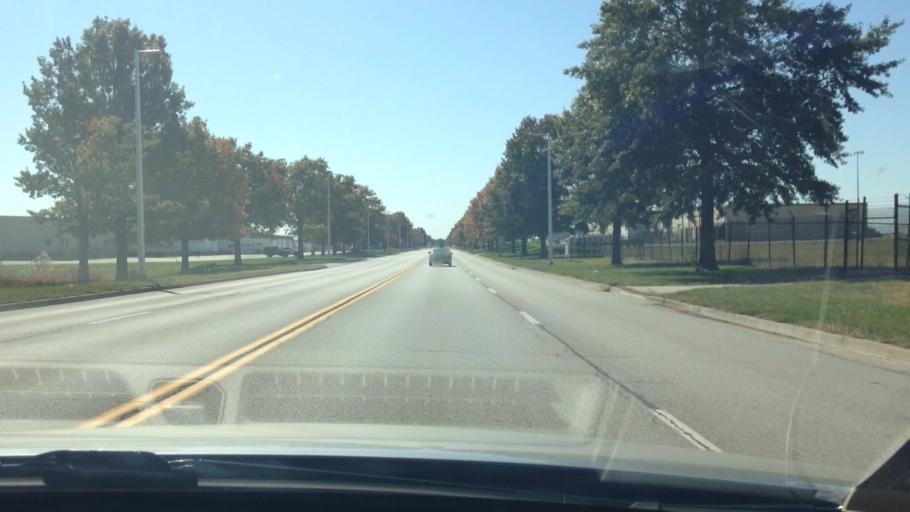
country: US
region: Missouri
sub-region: Platte County
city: Weatherby Lake
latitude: 39.3202
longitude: -94.7141
